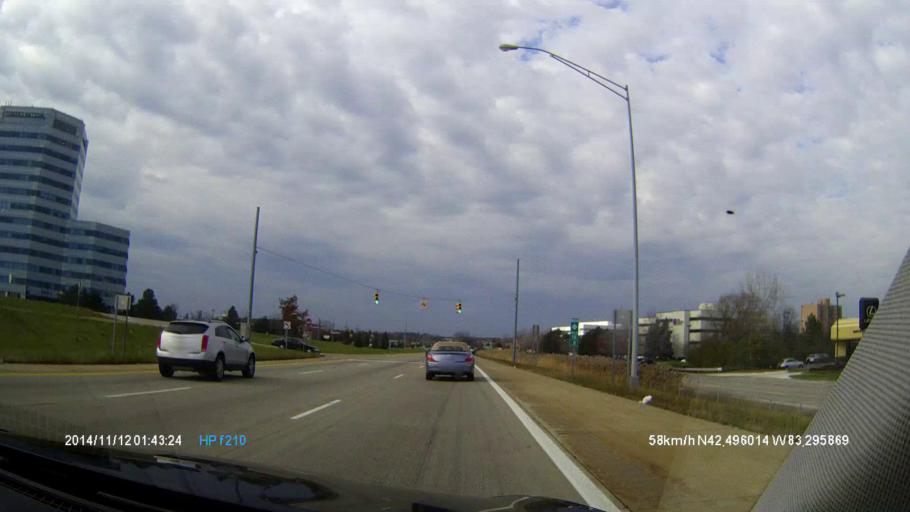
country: US
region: Michigan
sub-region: Oakland County
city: Franklin
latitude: 42.4961
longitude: -83.2960
